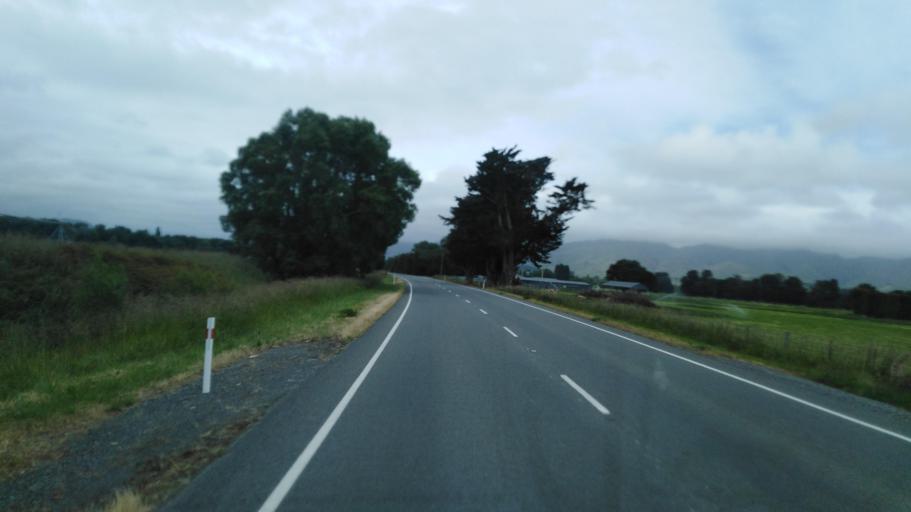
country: NZ
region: Canterbury
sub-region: Kaikoura District
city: Kaikoura
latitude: -42.7359
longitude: 173.2708
